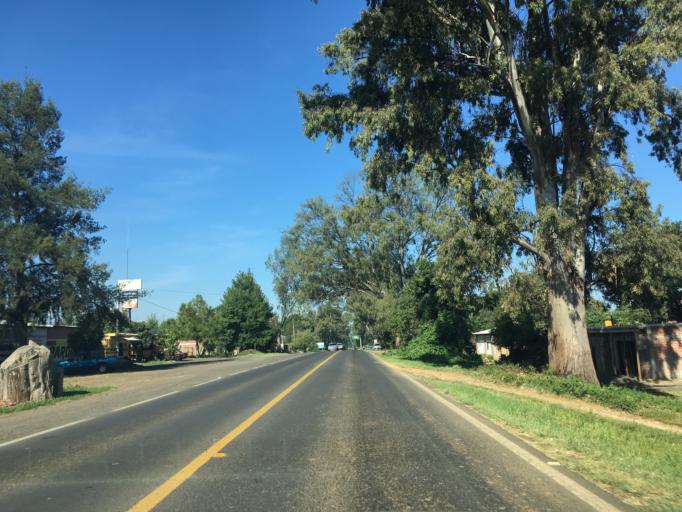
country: MX
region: Mexico
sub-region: Chalco
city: Santo Tomas
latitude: 19.8438
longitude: -102.0869
